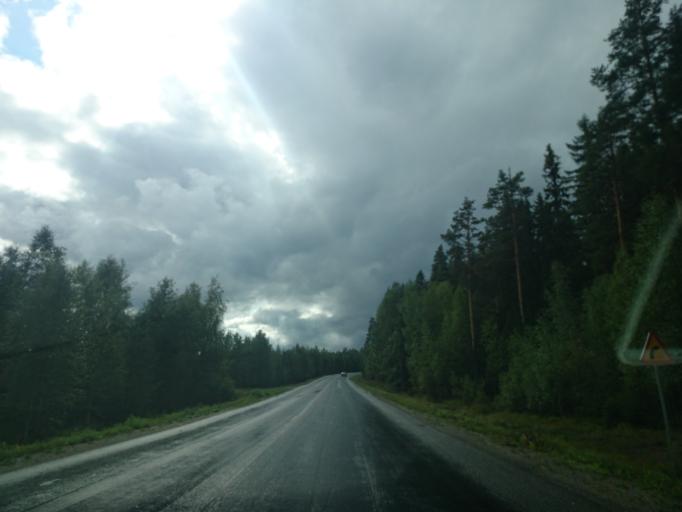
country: SE
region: Vaesternorrland
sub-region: Ange Kommun
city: Ange
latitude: 62.4051
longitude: 15.4830
